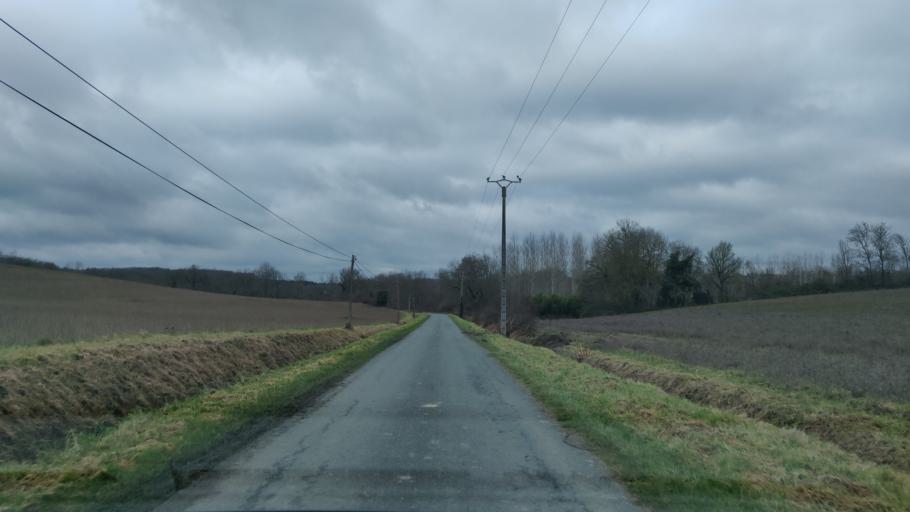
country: FR
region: Aquitaine
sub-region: Departement du Lot-et-Garonne
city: Saint-Hilaire
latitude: 44.5782
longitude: 0.7126
